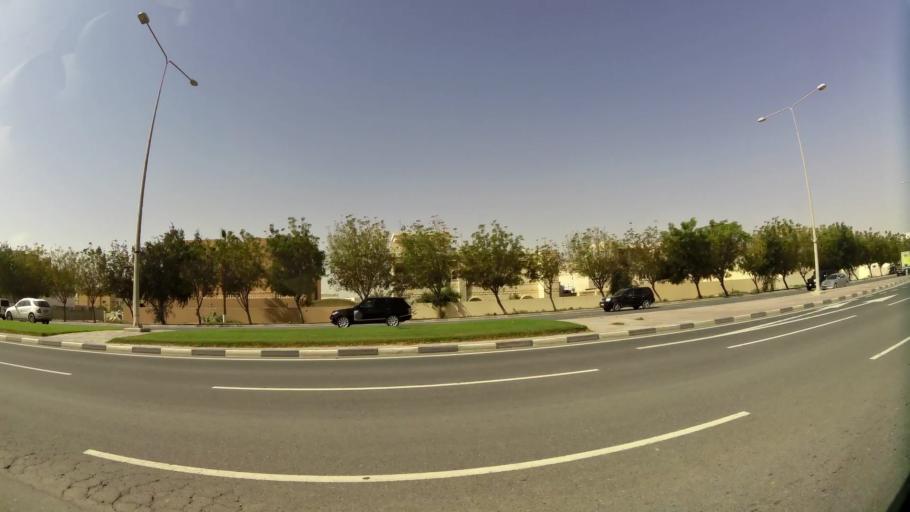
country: QA
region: Baladiyat ad Dawhah
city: Doha
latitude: 25.3542
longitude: 51.4971
